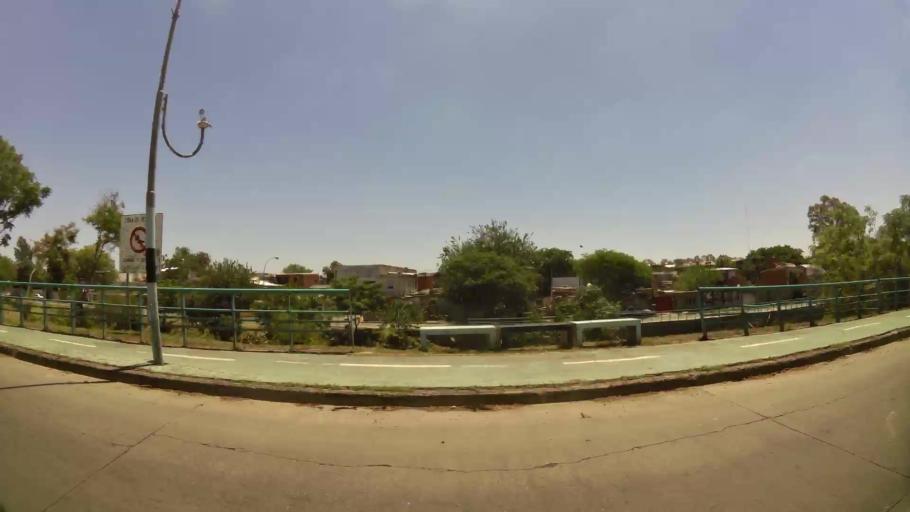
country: AR
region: Cordoba
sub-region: Departamento de Capital
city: Cordoba
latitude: -31.3987
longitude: -64.2030
